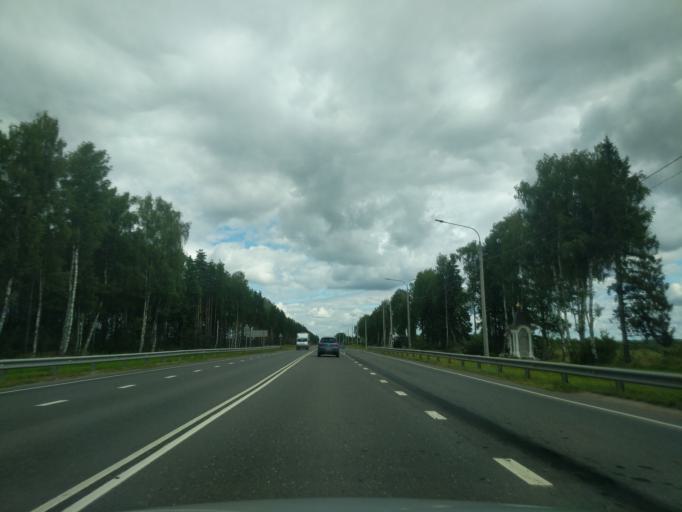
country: RU
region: Jaroslavl
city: Nekrasovskoye
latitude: 57.6097
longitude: 40.3347
